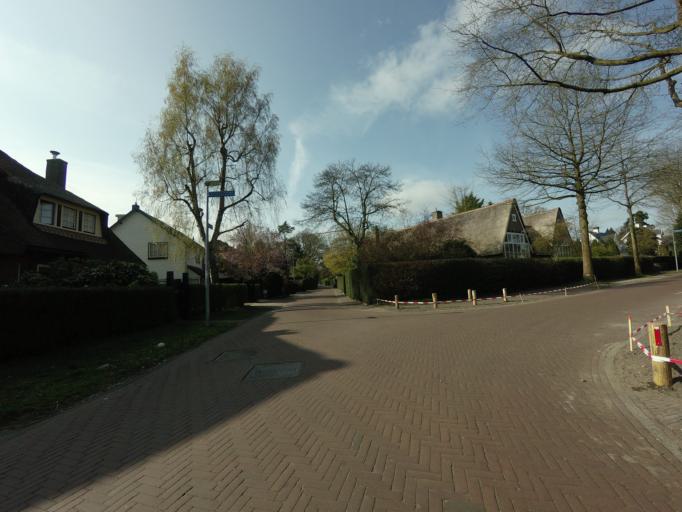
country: NL
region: North Holland
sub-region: Gemeente Laren
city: Laren
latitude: 52.2540
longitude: 5.2212
